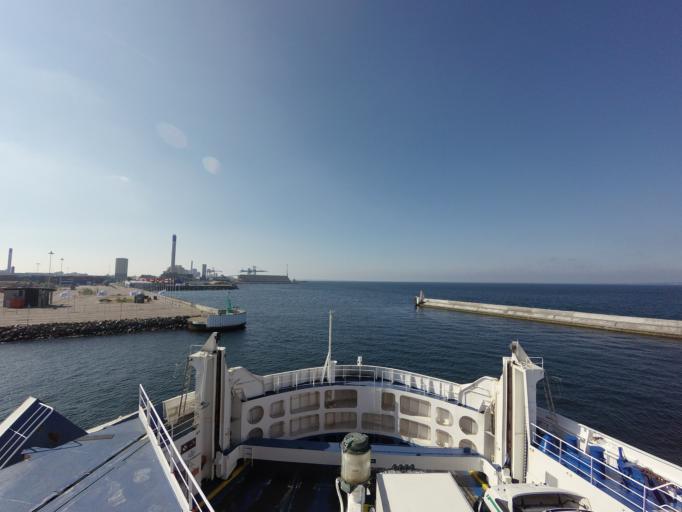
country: SE
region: Skane
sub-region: Helsingborg
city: Helsingborg
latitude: 56.0407
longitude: 12.6875
